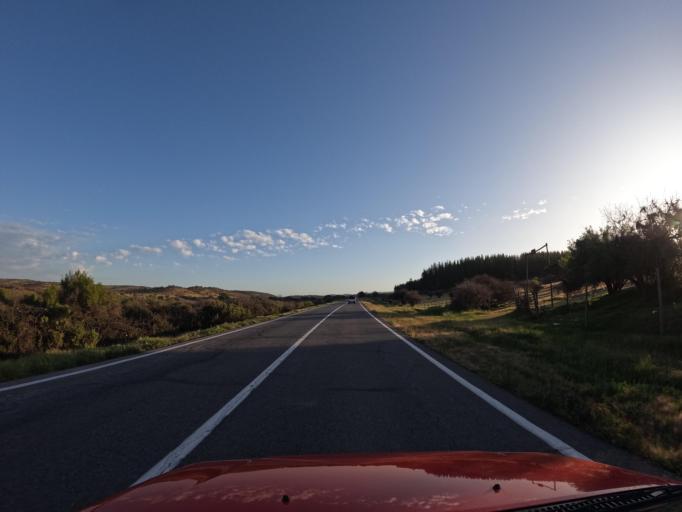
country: CL
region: O'Higgins
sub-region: Provincia de Colchagua
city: Santa Cruz
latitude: -34.2979
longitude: -71.7326
